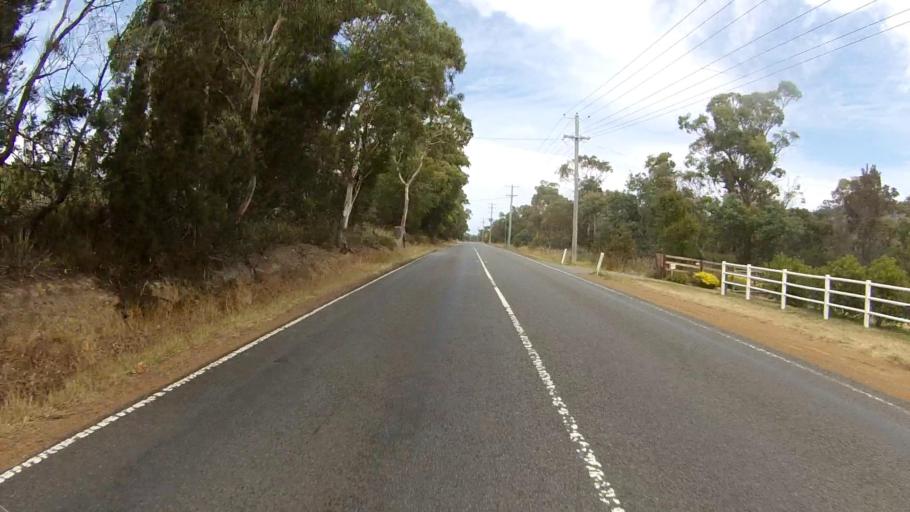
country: AU
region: Tasmania
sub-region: Clarence
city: Acton Park
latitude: -42.8697
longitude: 147.4837
